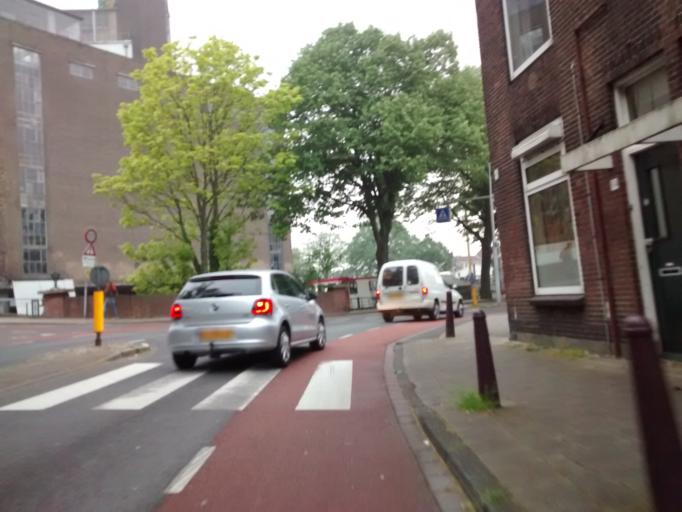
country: NL
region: South Holland
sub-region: Gemeente Leiden
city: Leiden
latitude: 52.1581
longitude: 4.5045
